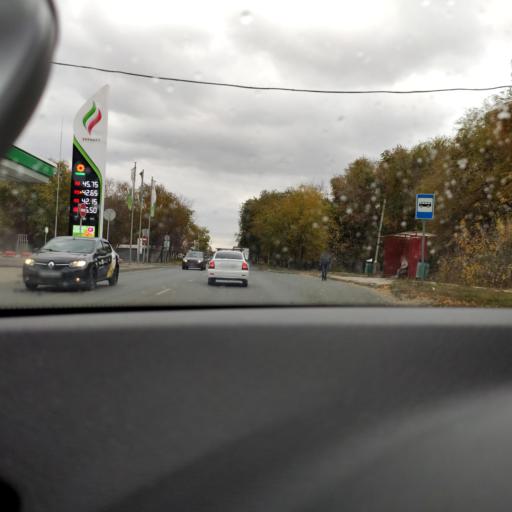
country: RU
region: Samara
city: Petra-Dubrava
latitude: 53.2475
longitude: 50.2690
